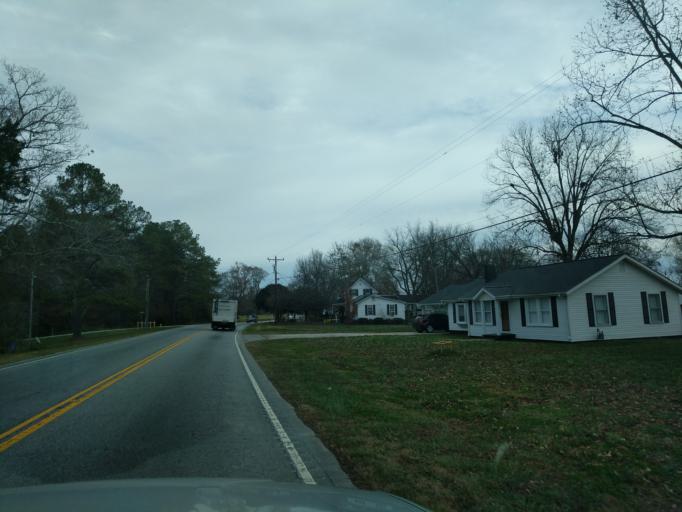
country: US
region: South Carolina
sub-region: Anderson County
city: Williamston
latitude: 34.6633
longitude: -82.5106
